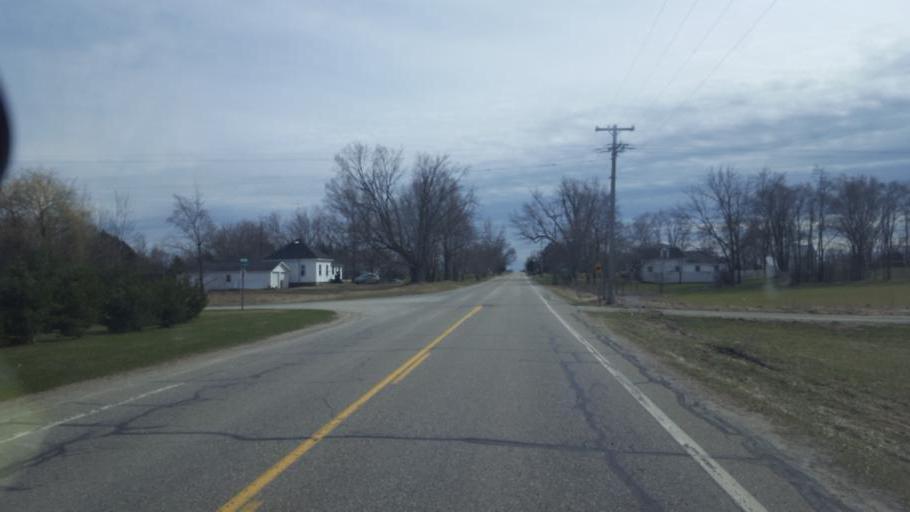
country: US
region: Michigan
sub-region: Montcalm County
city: Edmore
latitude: 43.4591
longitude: -85.0442
